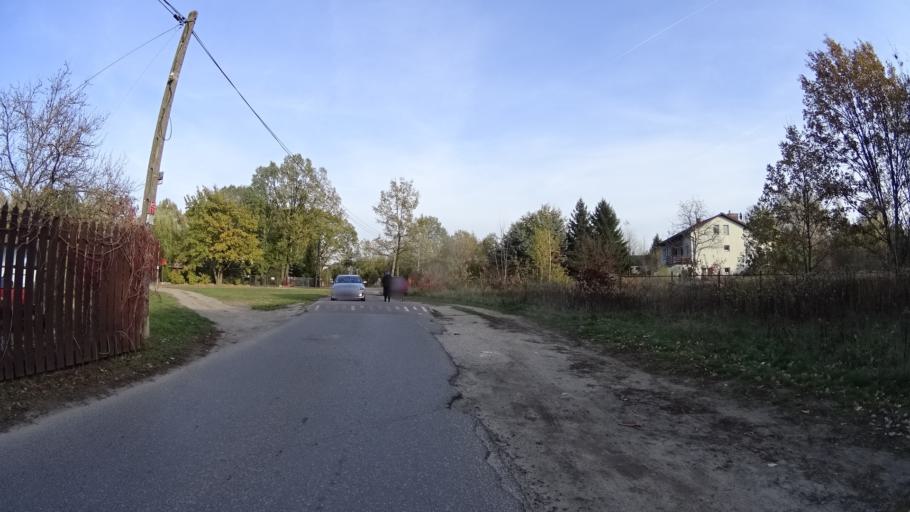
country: PL
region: Masovian Voivodeship
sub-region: Powiat warszawski zachodni
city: Lomianki
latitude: 52.2947
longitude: 20.8847
